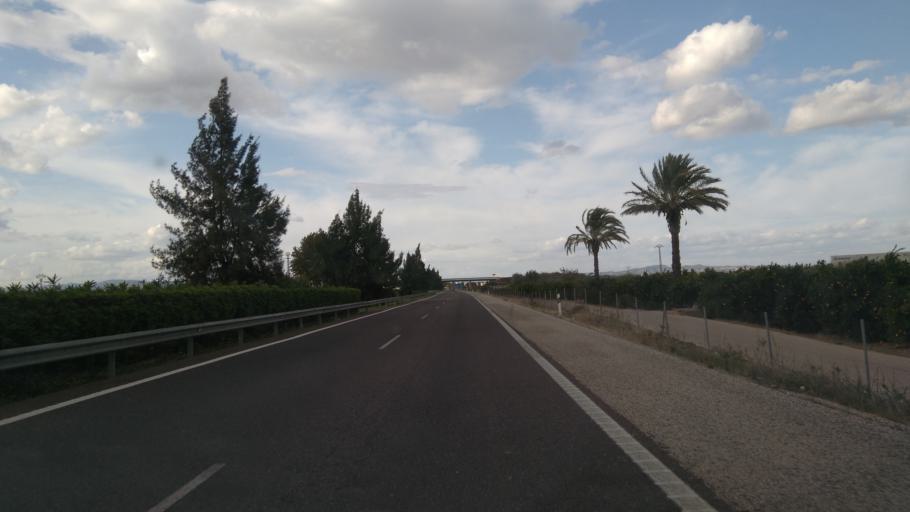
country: ES
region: Valencia
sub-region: Provincia de Valencia
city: Guadassuar
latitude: 39.1673
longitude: -0.4608
